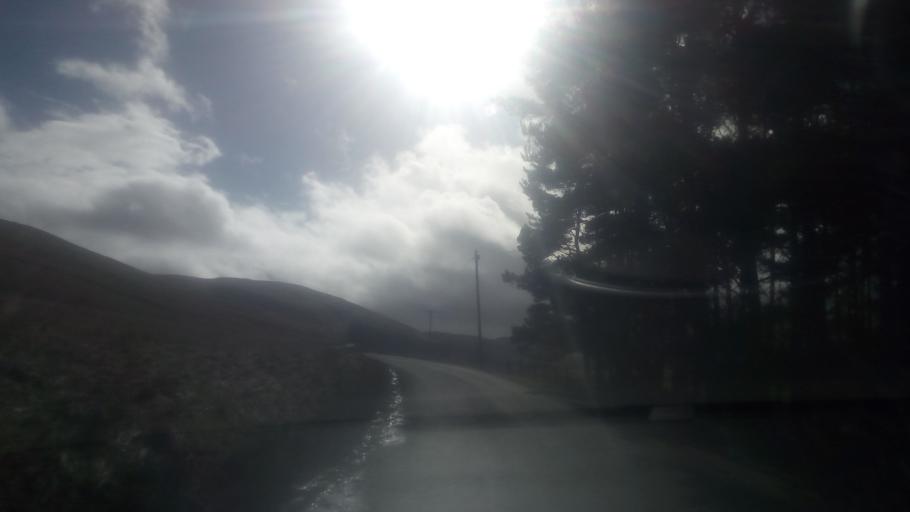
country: GB
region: Scotland
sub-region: The Scottish Borders
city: Innerleithen
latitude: 55.4996
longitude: -3.1167
